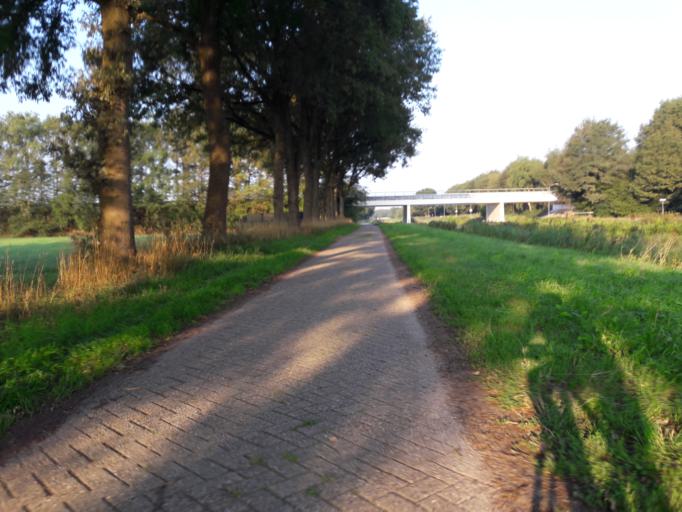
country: NL
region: Drenthe
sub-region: Gemeente Borger-Odoorn
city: Borger
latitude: 52.9149
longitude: 6.7938
